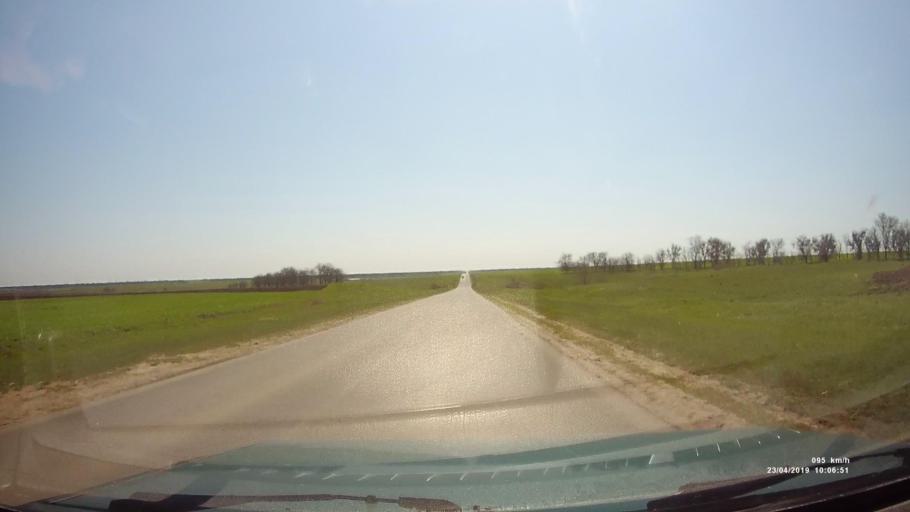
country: RU
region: Rostov
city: Sovetskoye
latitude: 46.7307
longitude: 42.2430
